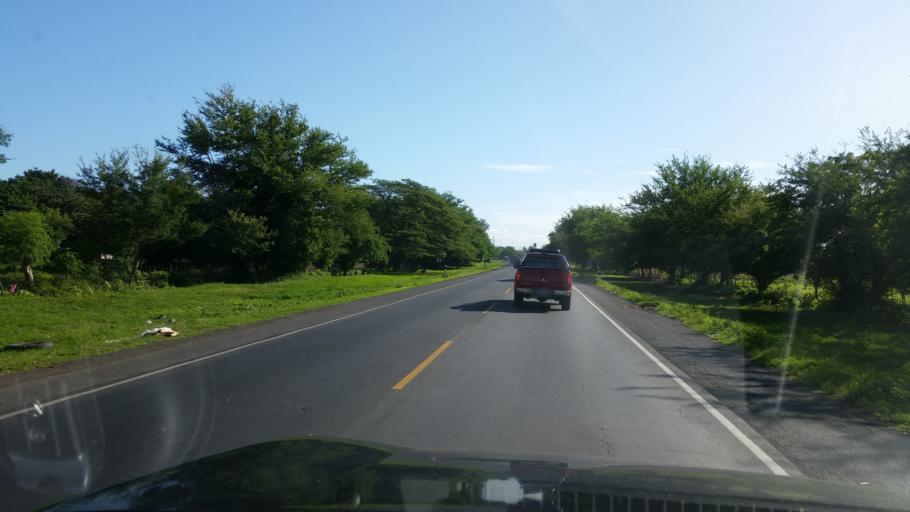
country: NI
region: Managua
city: Tipitapa
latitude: 12.1834
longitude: -86.1087
